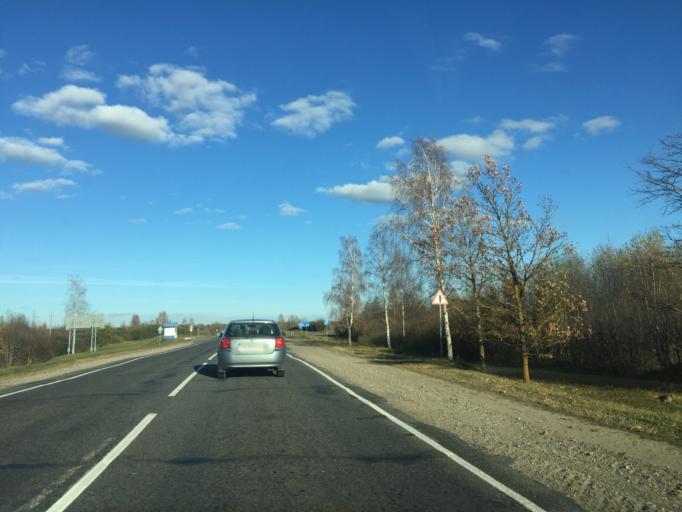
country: BY
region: Vitebsk
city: Dzisna
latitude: 55.2677
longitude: 28.1390
